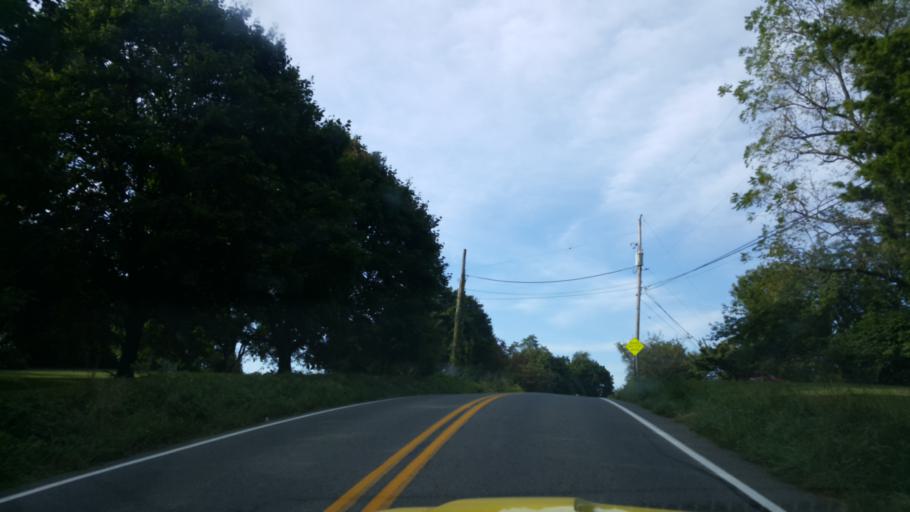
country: US
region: Pennsylvania
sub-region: Lebanon County
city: Campbelltown
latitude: 40.2577
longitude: -76.5727
